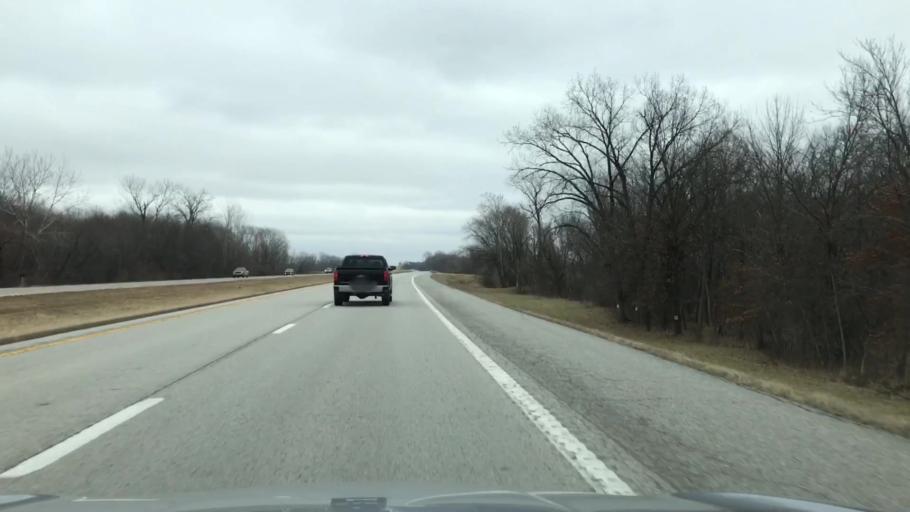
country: US
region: Missouri
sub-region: Livingston County
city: Chillicothe
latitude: 39.7768
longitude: -93.4393
